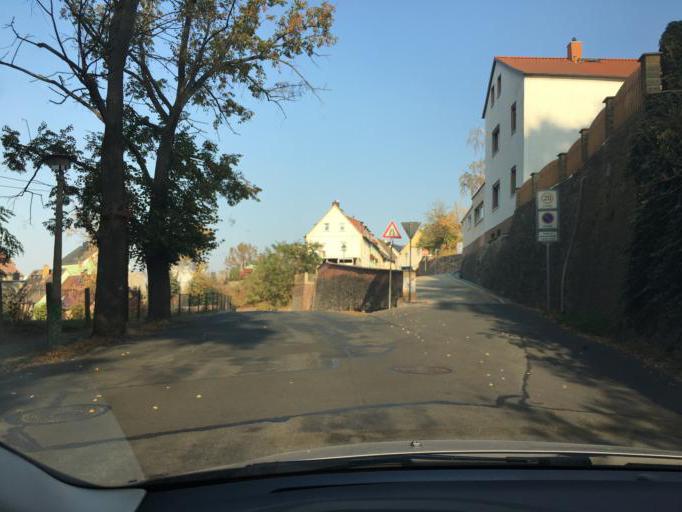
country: DE
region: Saxony
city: Wurzen
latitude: 51.3700
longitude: 12.7326
